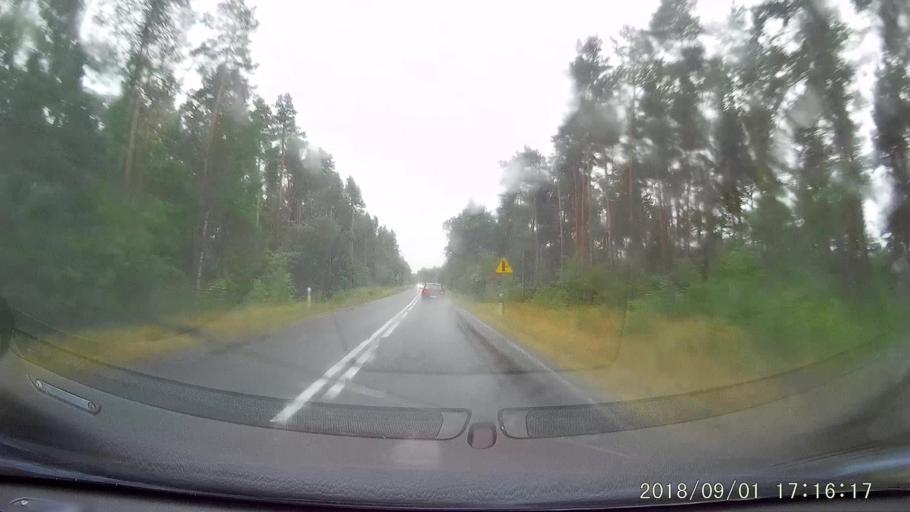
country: PL
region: Lubusz
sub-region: Powiat zielonogorski
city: Nowogrod Bobrzanski
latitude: 51.7645
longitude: 15.2688
